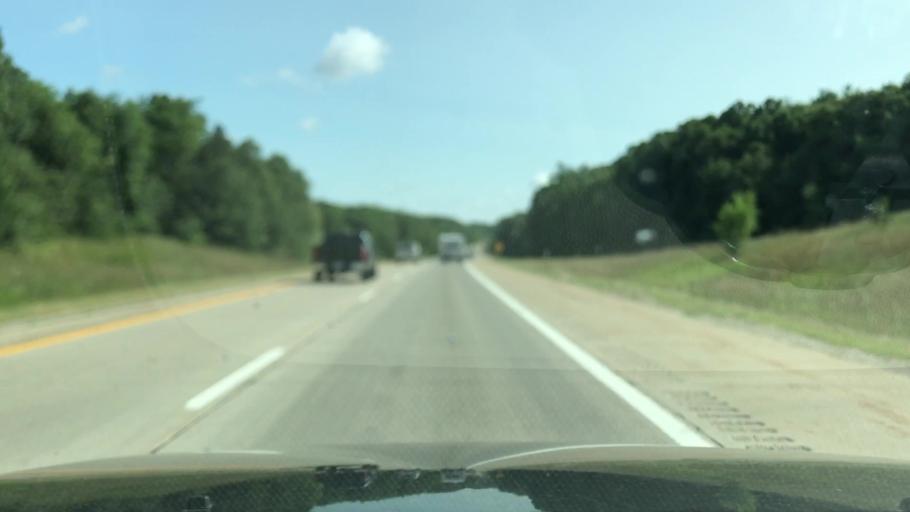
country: US
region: Michigan
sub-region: Kent County
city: Northview
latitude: 43.0908
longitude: -85.6304
